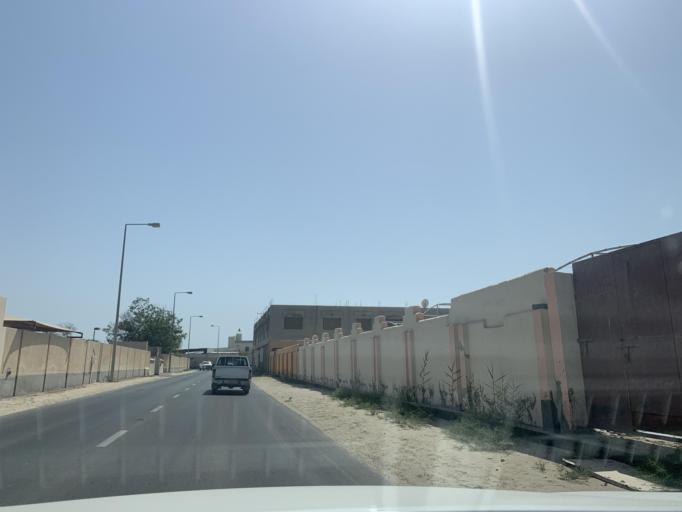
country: BH
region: Manama
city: Jidd Hafs
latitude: 26.2284
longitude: 50.4642
